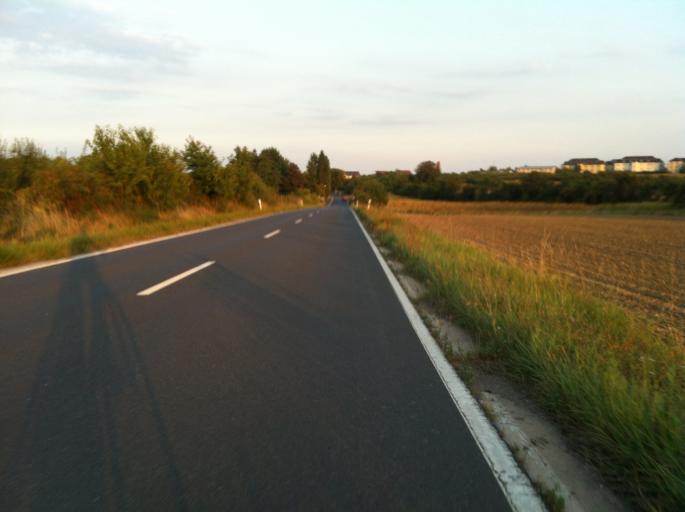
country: DE
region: Rheinland-Pfalz
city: Wackernheim
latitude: 49.9749
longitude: 8.1078
